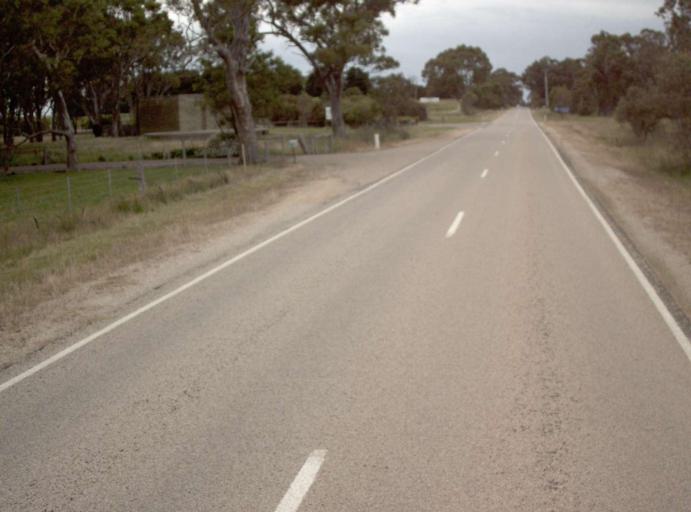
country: AU
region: Victoria
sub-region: East Gippsland
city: Bairnsdale
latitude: -37.8773
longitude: 147.5597
